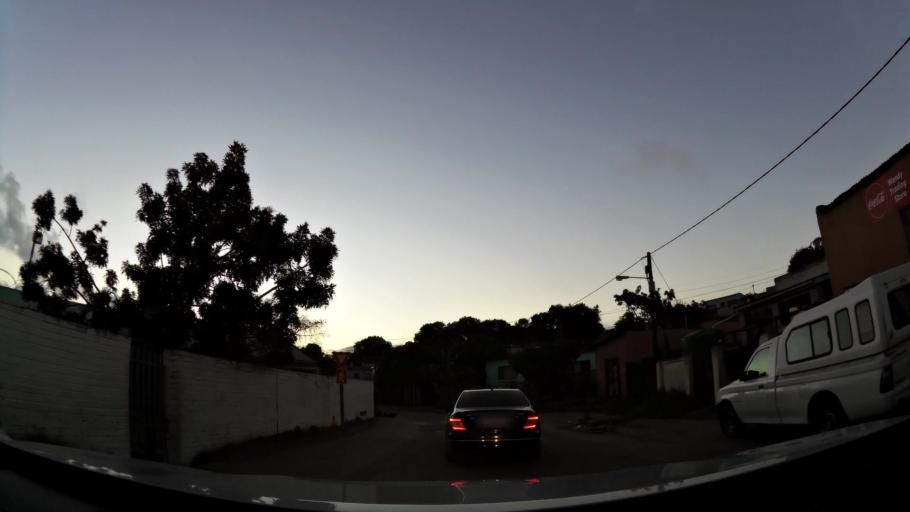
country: ZA
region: Western Cape
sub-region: Eden District Municipality
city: Knysna
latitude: -34.0271
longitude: 22.8192
